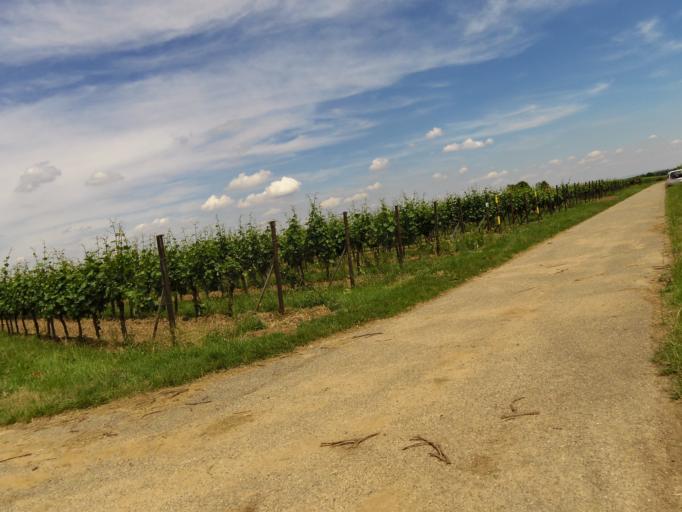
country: DE
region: Rheinland-Pfalz
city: Roschbach
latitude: 49.2427
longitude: 8.1193
